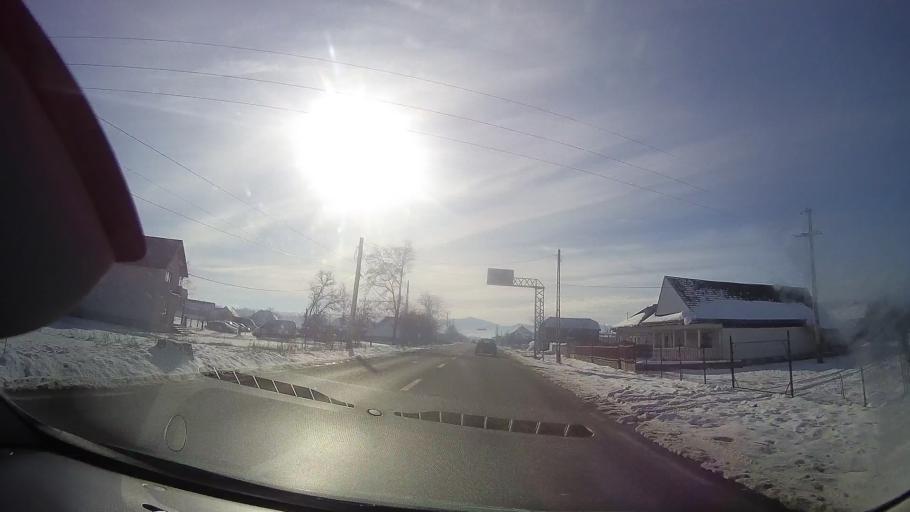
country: RO
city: Vanatori-Neamt
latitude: 47.1752
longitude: 26.3264
